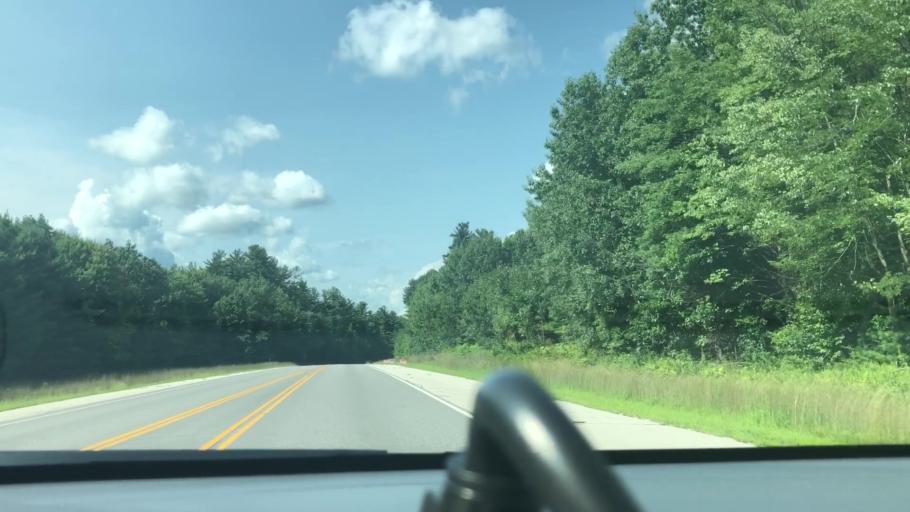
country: US
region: New Hampshire
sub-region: Hillsborough County
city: Pinardville
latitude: 42.9922
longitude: -71.5245
